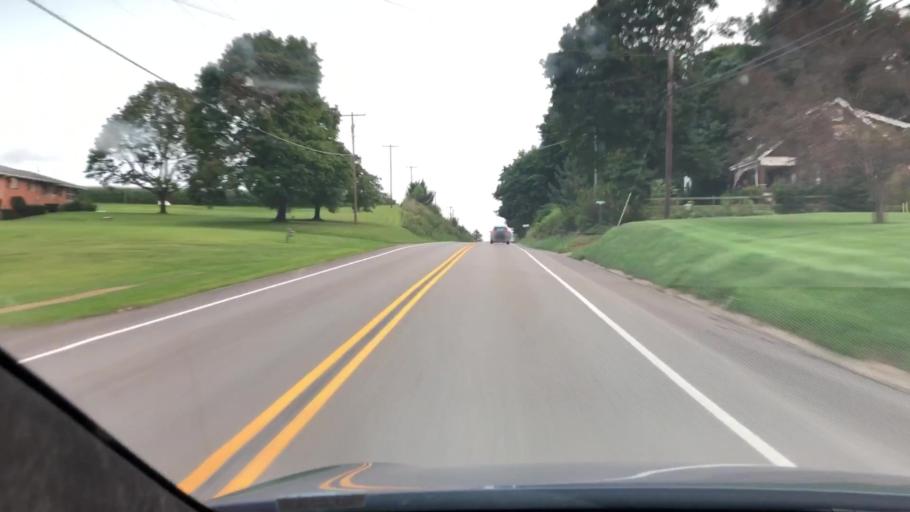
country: US
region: Pennsylvania
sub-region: Butler County
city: Slippery Rock
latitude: 41.1151
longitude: -80.0071
